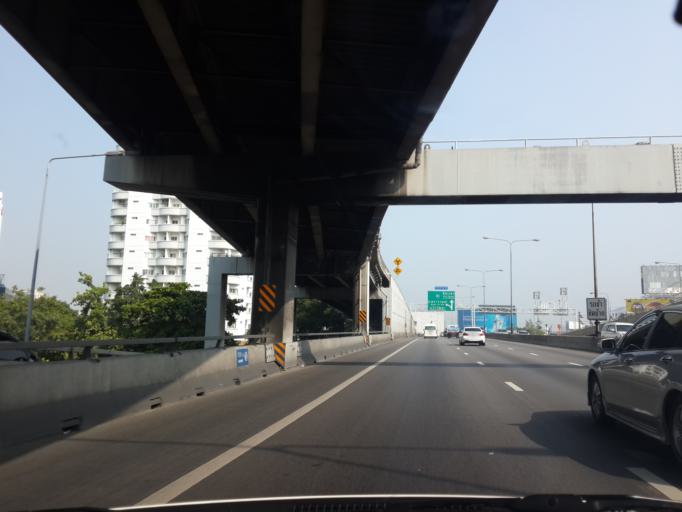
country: TH
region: Bangkok
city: Ratchathewi
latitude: 13.7474
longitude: 100.5500
